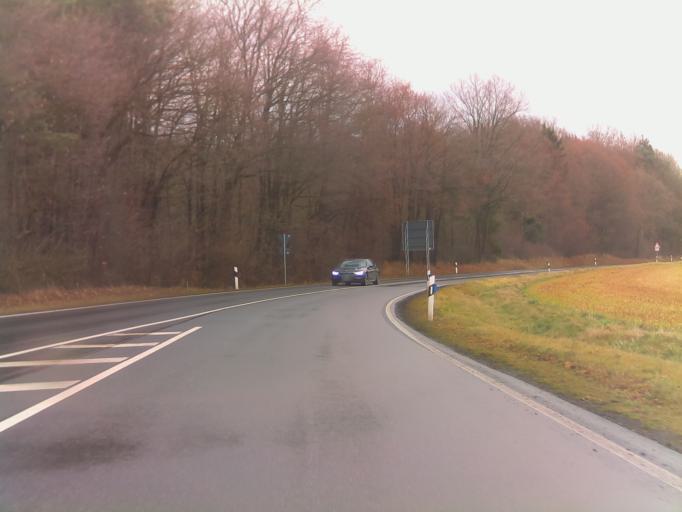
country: DE
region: Hesse
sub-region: Regierungsbezirk Giessen
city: Lauterbach
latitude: 50.6265
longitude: 9.3570
